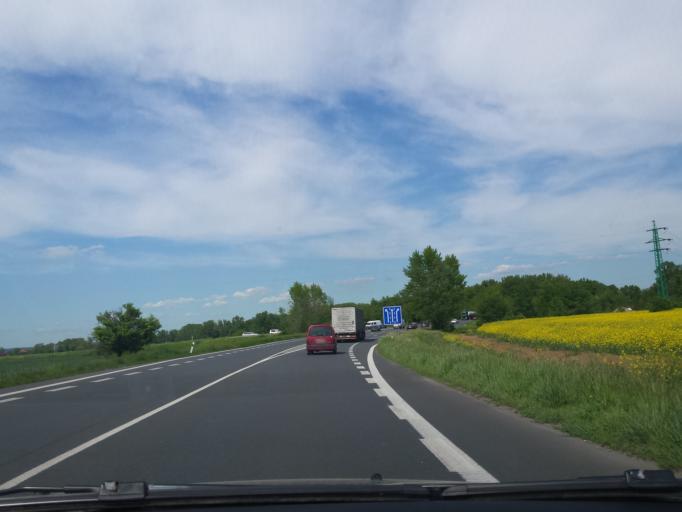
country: CZ
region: Central Bohemia
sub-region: Okres Melnik
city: Melnik
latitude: 50.3547
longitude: 14.4538
